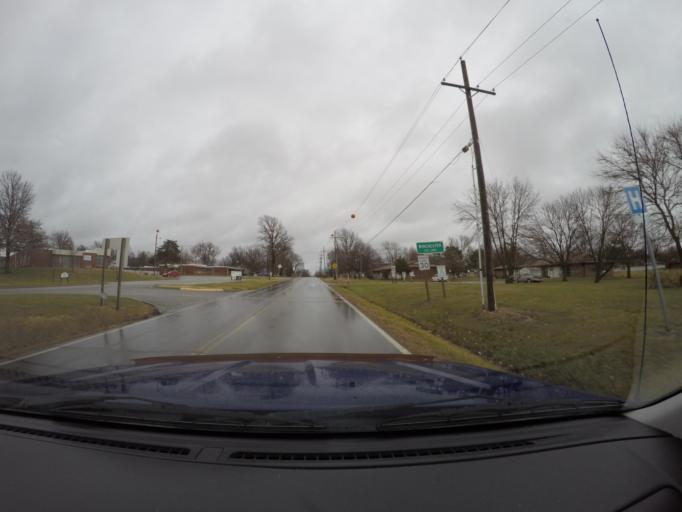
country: US
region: Kansas
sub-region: Jefferson County
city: Oskaloosa
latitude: 39.3253
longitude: -95.2712
